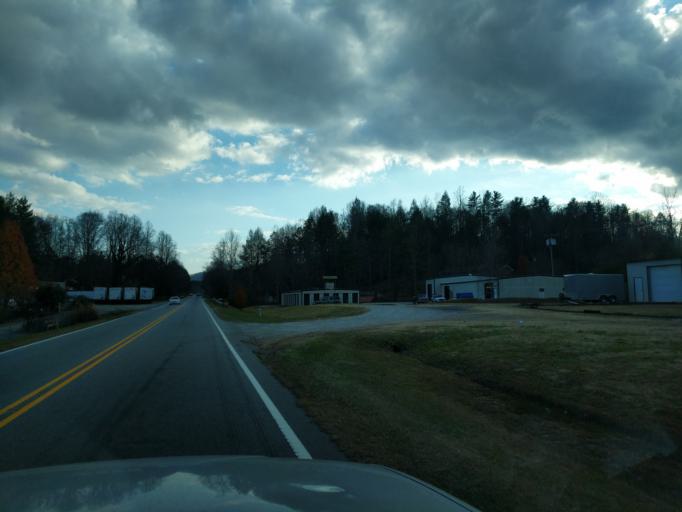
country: US
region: North Carolina
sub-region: McDowell County
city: West Marion
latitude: 35.5990
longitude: -81.9841
